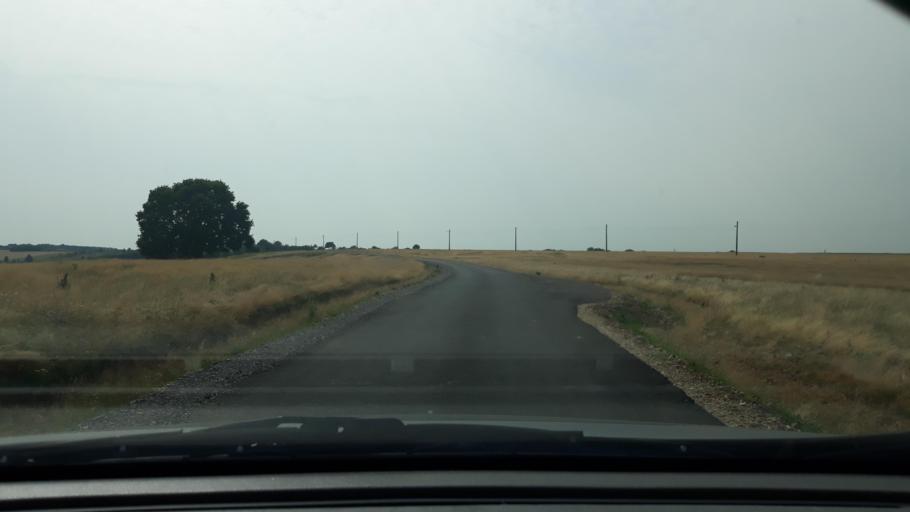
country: RO
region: Bihor
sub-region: Comuna Tauteu
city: Tauteu
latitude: 47.2664
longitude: 22.3170
